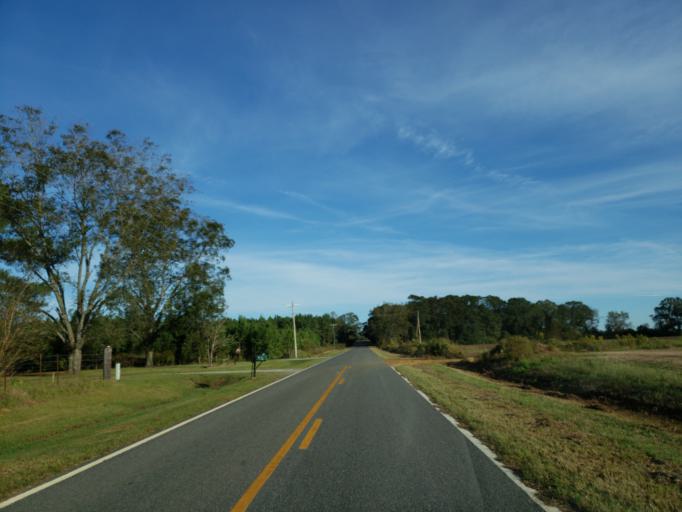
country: US
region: Georgia
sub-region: Crisp County
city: Cordele
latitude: 32.0315
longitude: -83.7487
